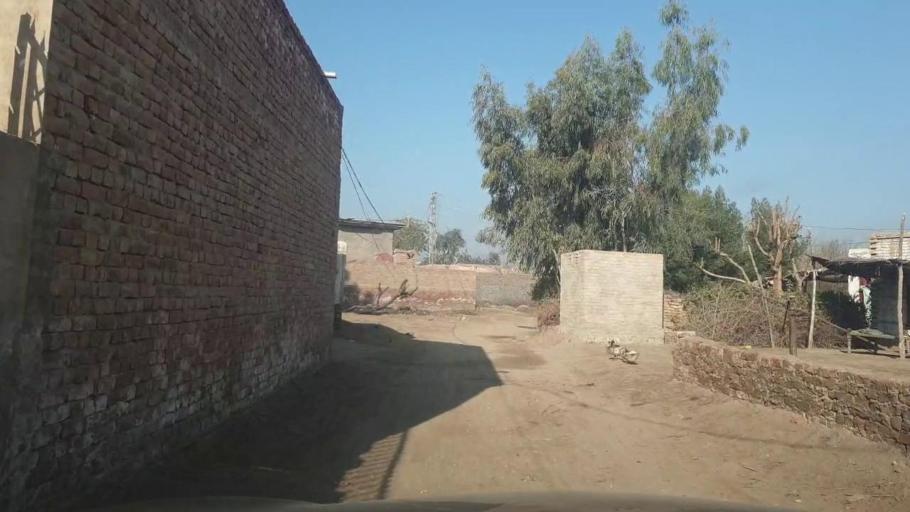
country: PK
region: Sindh
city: Mirpur Mathelo
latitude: 28.0776
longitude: 69.4679
